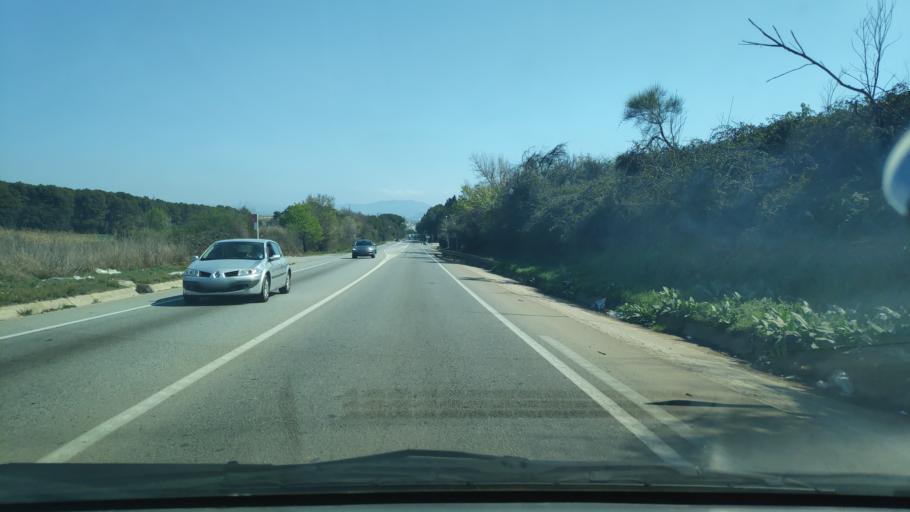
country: ES
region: Catalonia
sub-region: Provincia de Barcelona
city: Polinya
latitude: 41.5317
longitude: 2.1399
